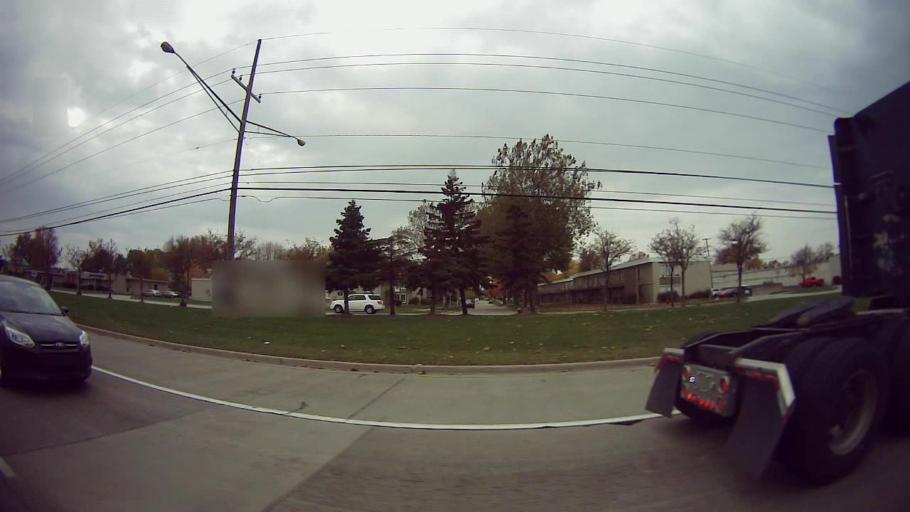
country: US
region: Michigan
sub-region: Macomb County
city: Sterling Heights
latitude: 42.5331
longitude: -83.0476
